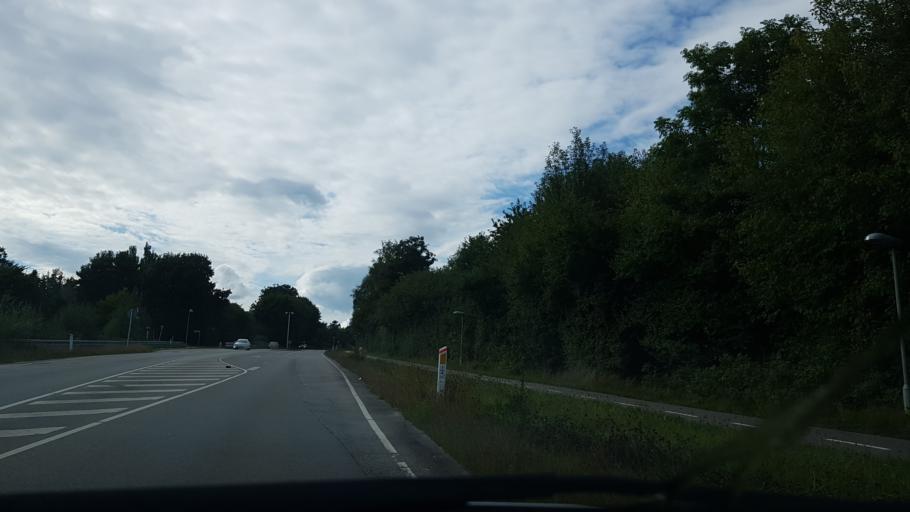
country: DK
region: Capital Region
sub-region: Fredensborg Kommune
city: Humlebaek
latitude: 55.9835
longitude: 12.5292
